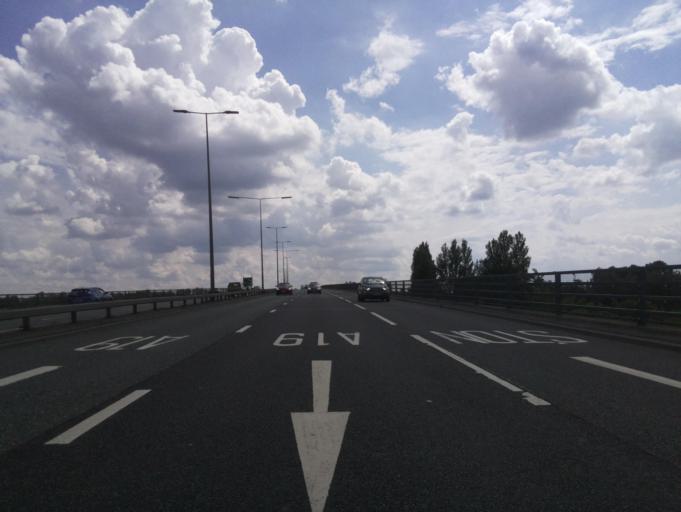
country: GB
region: England
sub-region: Stockton-on-Tees
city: Billingham
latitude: 54.5719
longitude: -1.2700
